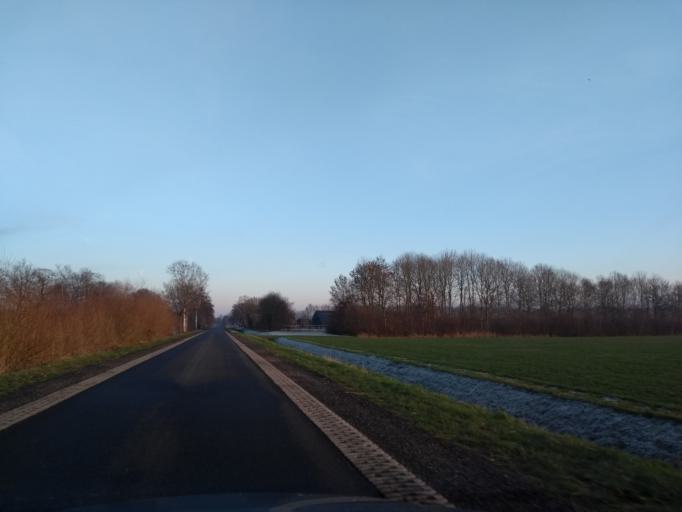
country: NL
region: Overijssel
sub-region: Gemeente Twenterand
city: Den Ham
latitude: 52.4340
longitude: 6.4948
